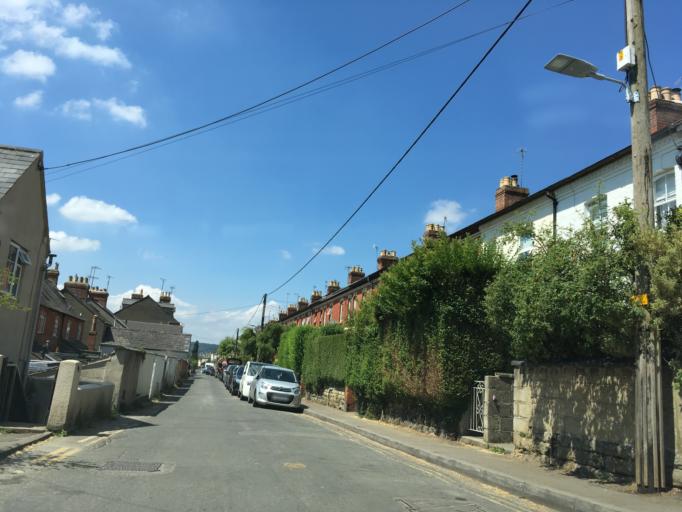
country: GB
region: England
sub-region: Gloucestershire
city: Stroud
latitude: 51.7417
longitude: -2.2035
